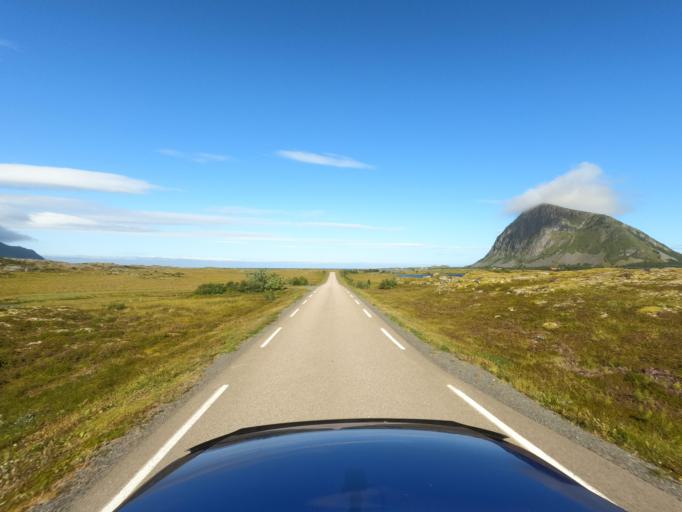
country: NO
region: Nordland
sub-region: Vestvagoy
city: Evjen
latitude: 68.3127
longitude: 14.0941
